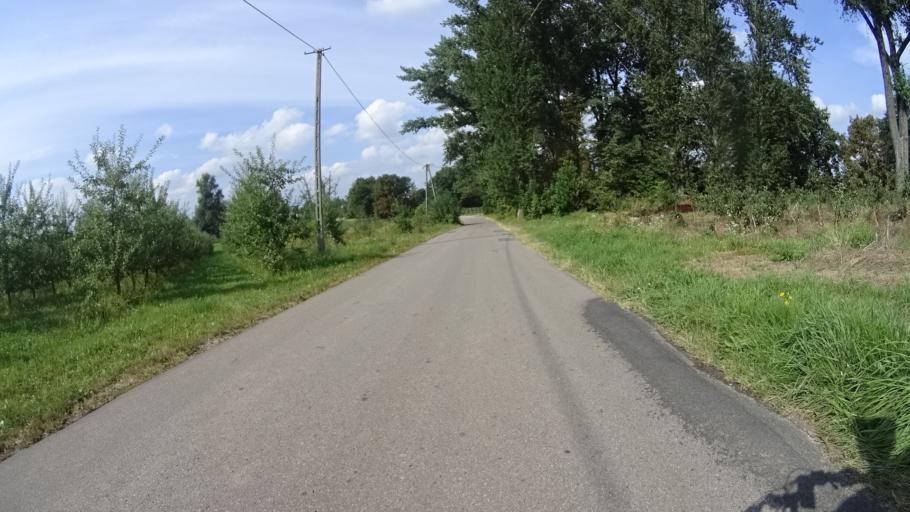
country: PL
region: Masovian Voivodeship
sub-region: Powiat grojecki
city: Goszczyn
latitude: 51.6983
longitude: 20.8479
